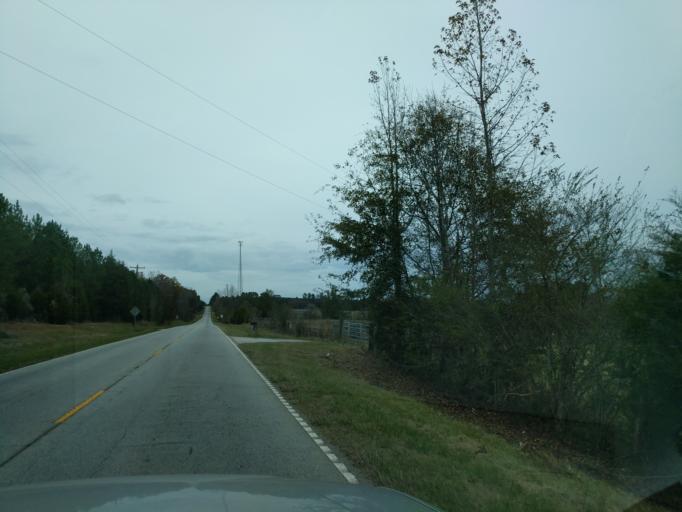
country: US
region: South Carolina
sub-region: Saluda County
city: Saluda
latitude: 34.0579
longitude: -81.7643
